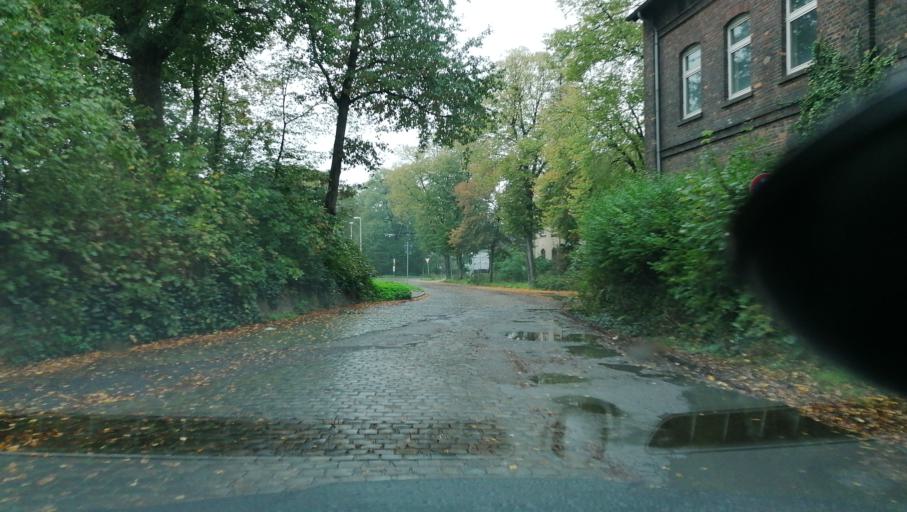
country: DE
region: North Rhine-Westphalia
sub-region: Regierungsbezirk Arnsberg
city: Herne
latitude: 51.5629
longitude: 7.1953
